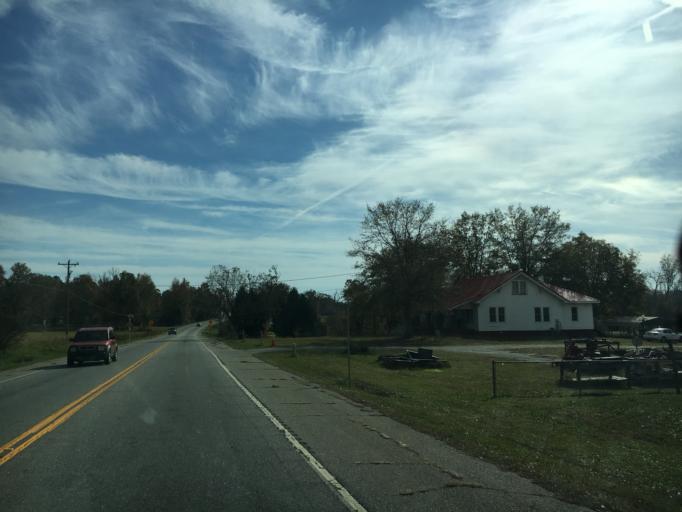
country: US
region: South Carolina
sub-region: Anderson County
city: Belton
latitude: 34.5729
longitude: -82.5503
